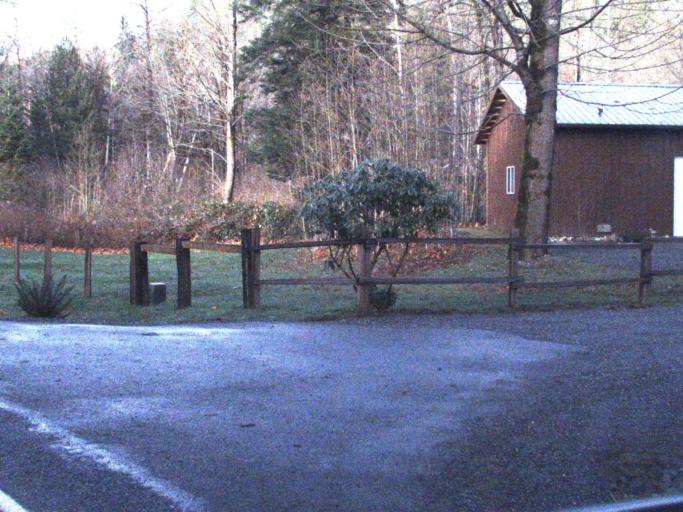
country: US
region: Washington
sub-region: Snohomish County
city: Darrington
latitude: 48.4362
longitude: -121.5749
